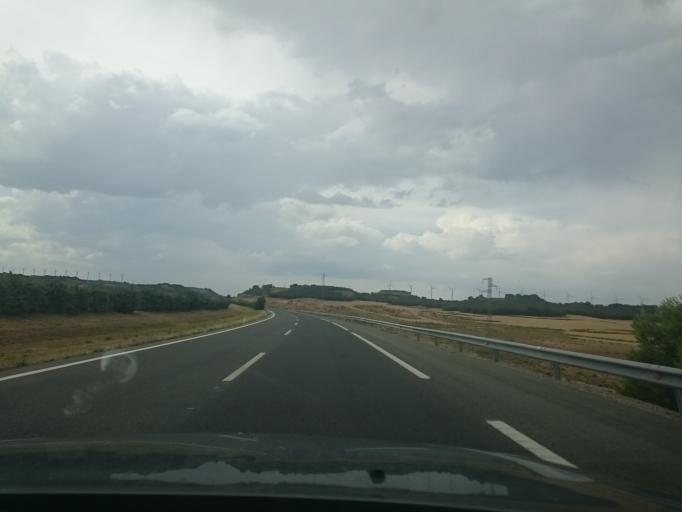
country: ES
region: Navarre
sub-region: Provincia de Navarra
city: Murchante
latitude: 42.0732
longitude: -1.6936
